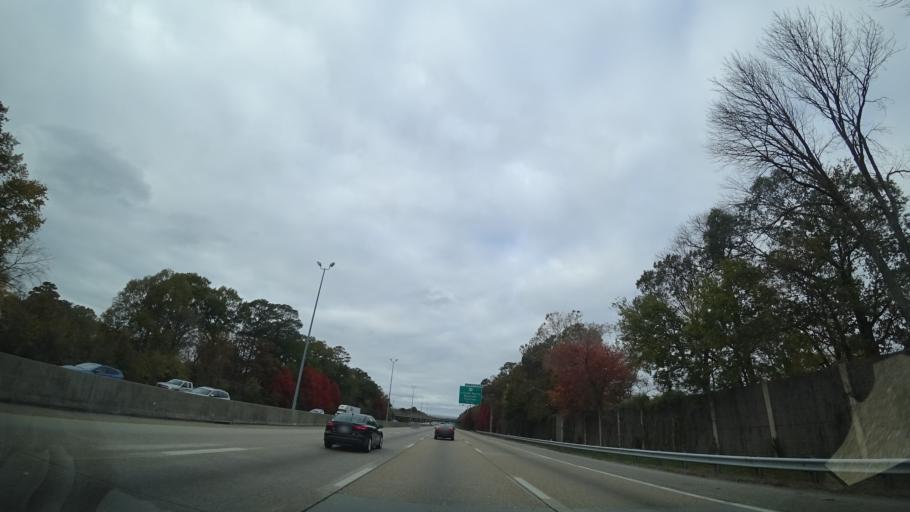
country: US
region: Virginia
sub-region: City of Newport News
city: Newport News
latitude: 37.0810
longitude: -76.4506
